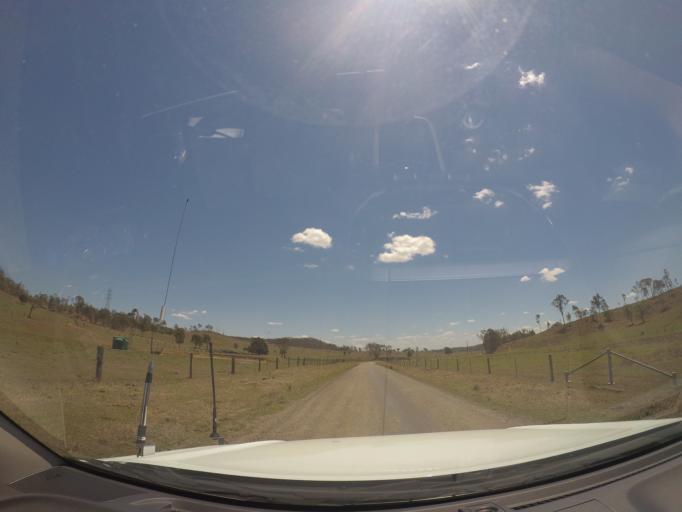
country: AU
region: Queensland
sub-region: Ipswich
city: Redbank Plains
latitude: -27.7480
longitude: 152.8308
